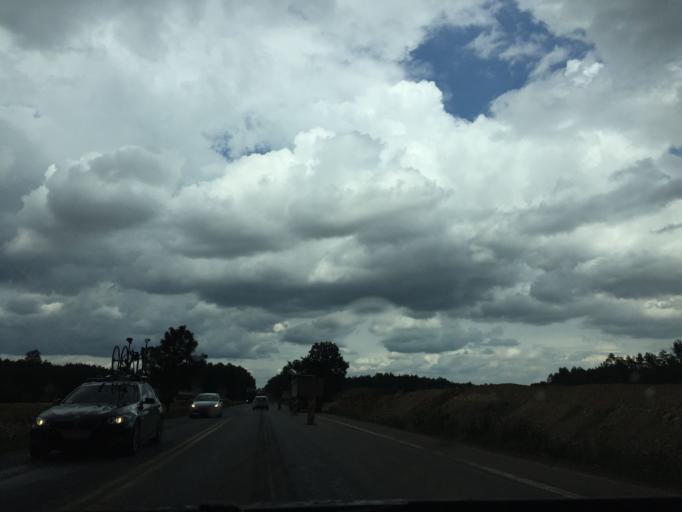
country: PL
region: Swietokrzyskie
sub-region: Powiat jedrzejowski
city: Jedrzejow
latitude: 50.6841
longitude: 20.3557
